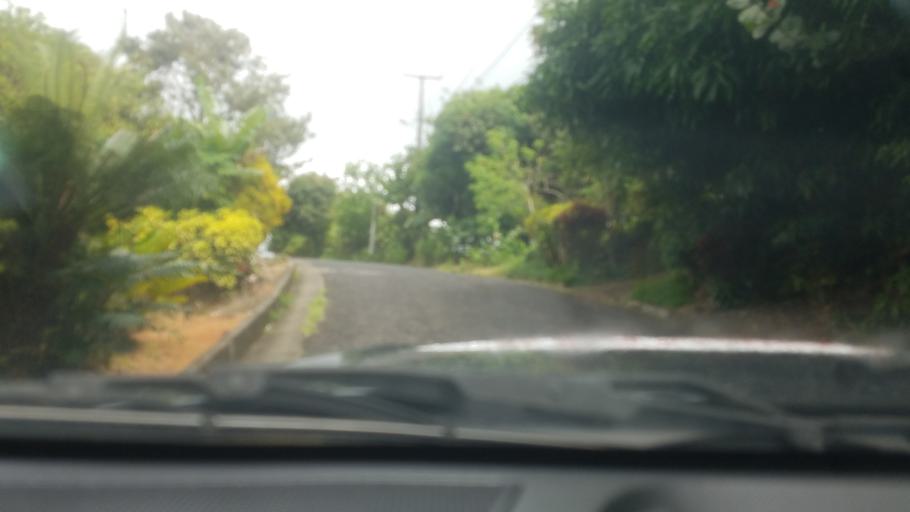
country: LC
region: Micoud Quarter
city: Micoud
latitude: 13.8107
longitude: -60.9499
